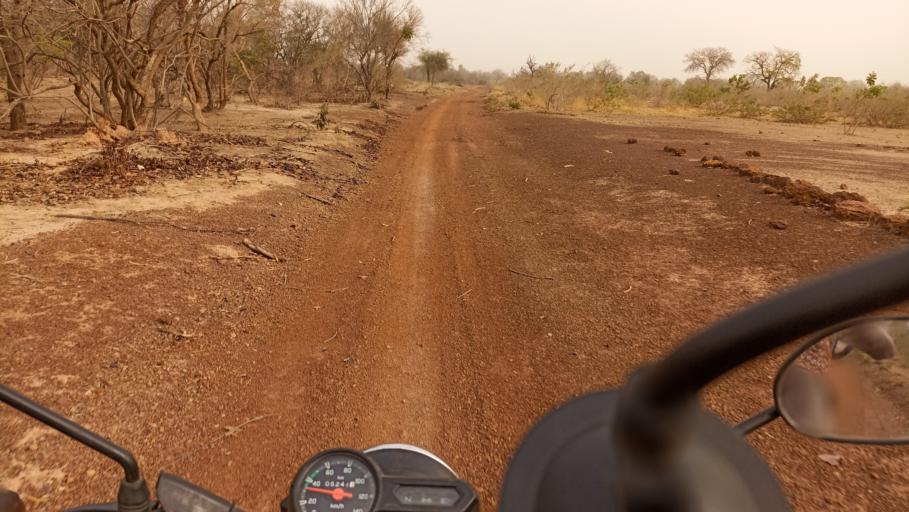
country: BF
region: Boucle du Mouhoun
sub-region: Province du Nayala
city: Toma
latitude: 12.8973
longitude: -2.7875
